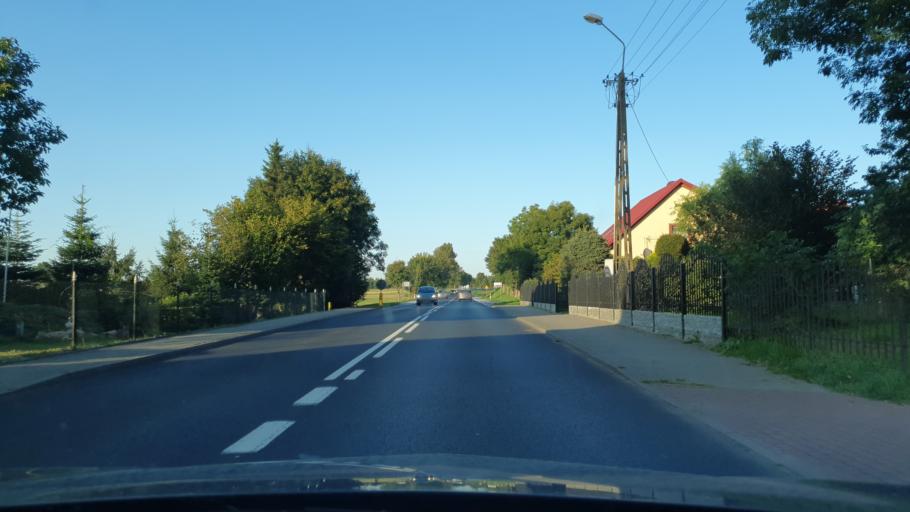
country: PL
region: West Pomeranian Voivodeship
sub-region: Powiat slawienski
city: Darlowo
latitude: 54.3114
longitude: 16.5200
